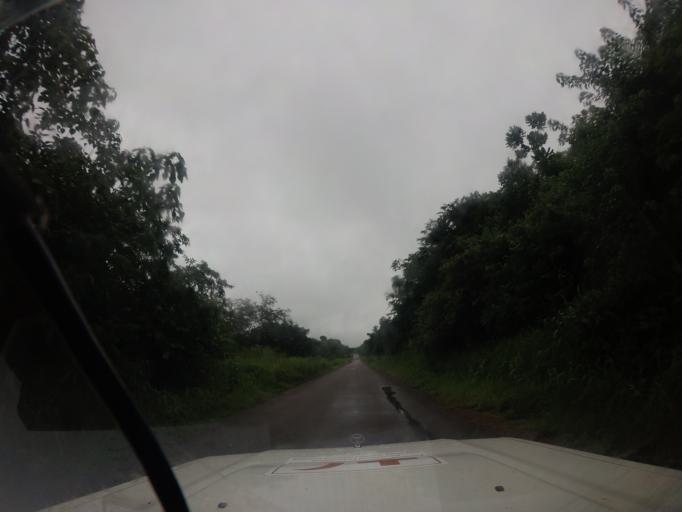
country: SL
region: Northern Province
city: Kabala
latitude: 9.5158
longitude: -11.5867
